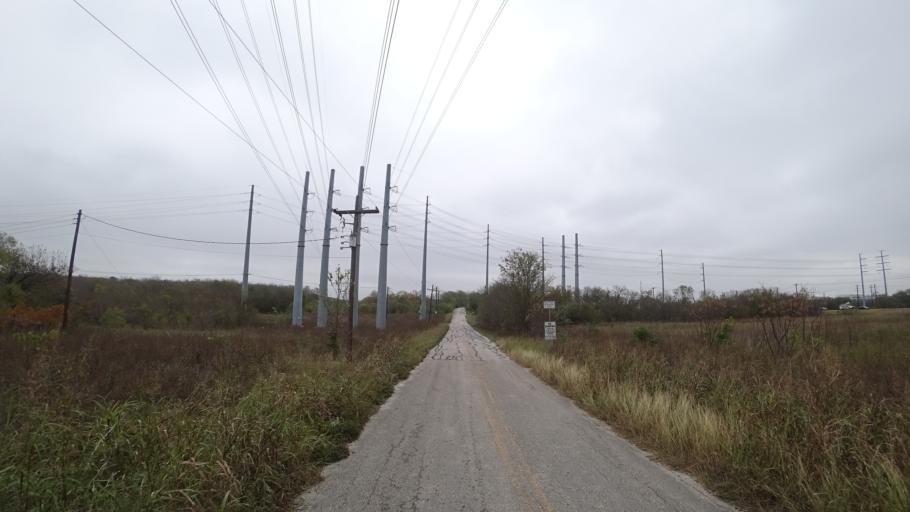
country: US
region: Texas
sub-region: Travis County
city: Pflugerville
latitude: 30.3838
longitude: -97.6417
